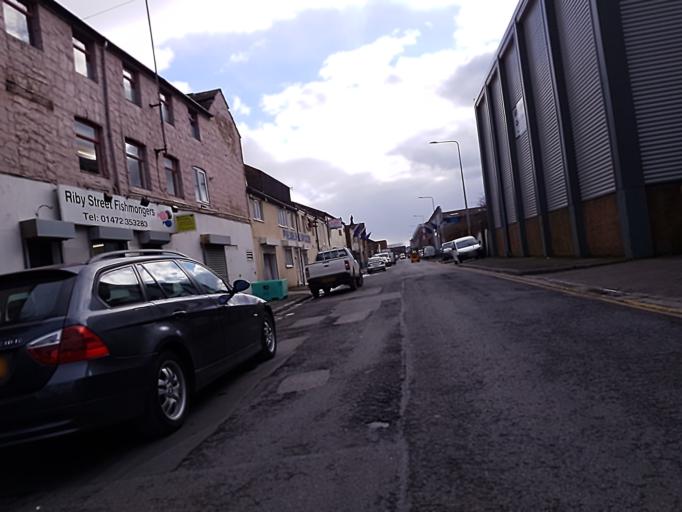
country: GB
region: England
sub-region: North East Lincolnshire
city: Grimsby
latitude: 53.5756
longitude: -0.0696
